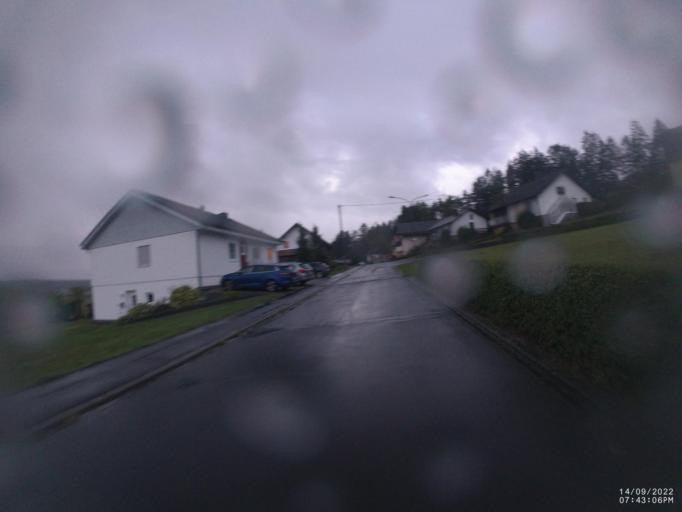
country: DE
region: Rheinland-Pfalz
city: Nohn
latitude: 50.3289
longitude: 6.7831
